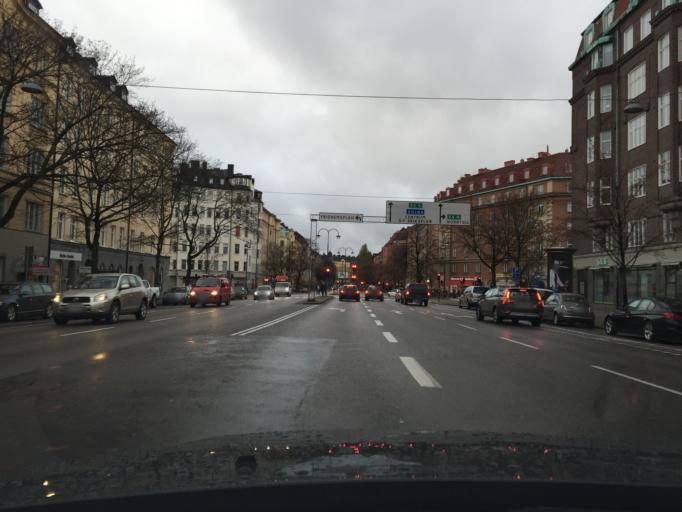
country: SE
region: Stockholm
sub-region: Stockholms Kommun
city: Stockholm
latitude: 59.3426
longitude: 18.0401
